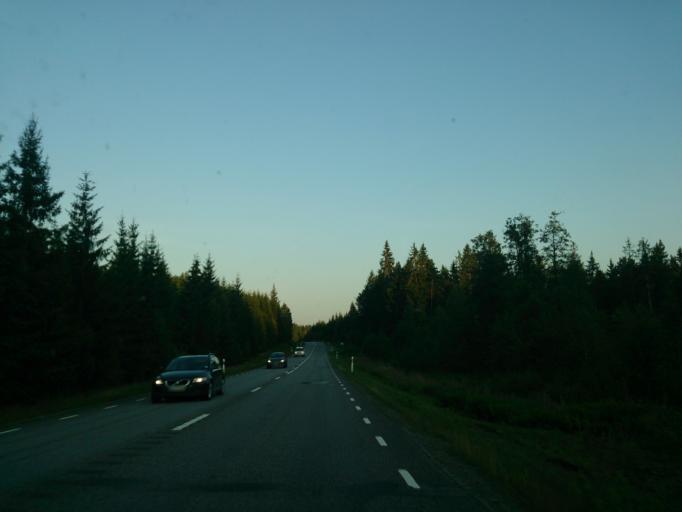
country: SE
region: Joenkoeping
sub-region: Varnamo Kommun
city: Rydaholm
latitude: 56.9445
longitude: 14.3617
